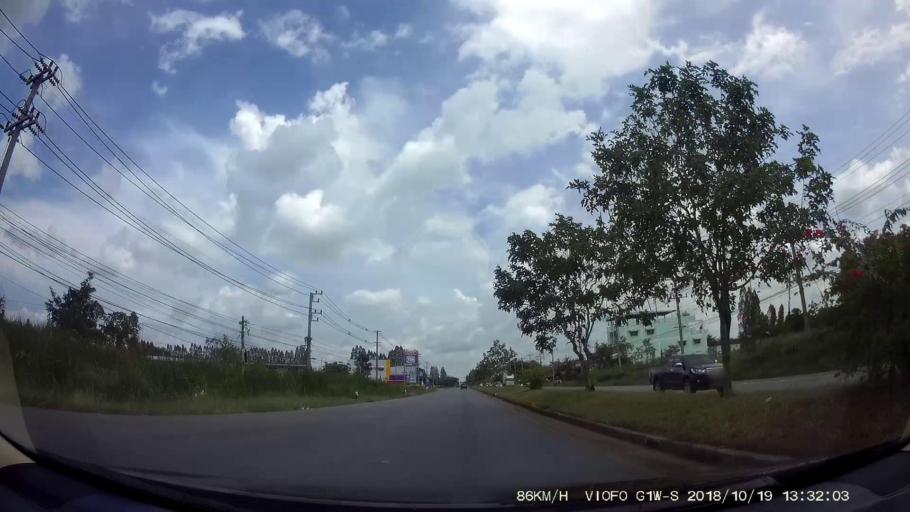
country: TH
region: Chaiyaphum
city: Chatturat
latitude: 15.5789
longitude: 101.8759
